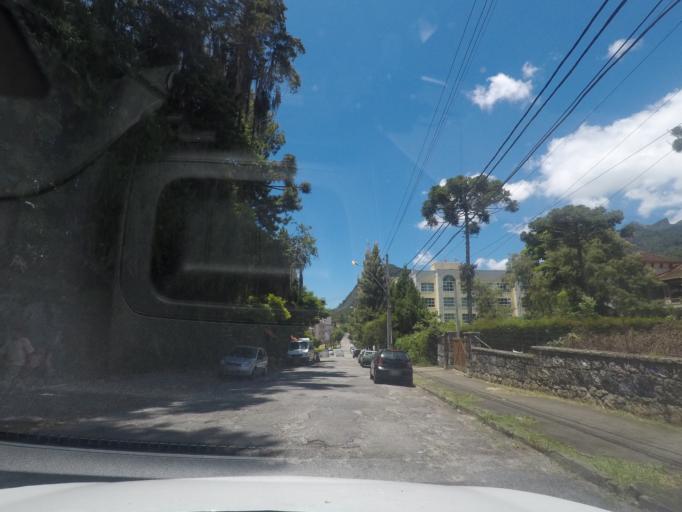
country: BR
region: Rio de Janeiro
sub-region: Teresopolis
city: Teresopolis
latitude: -22.4363
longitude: -42.9801
